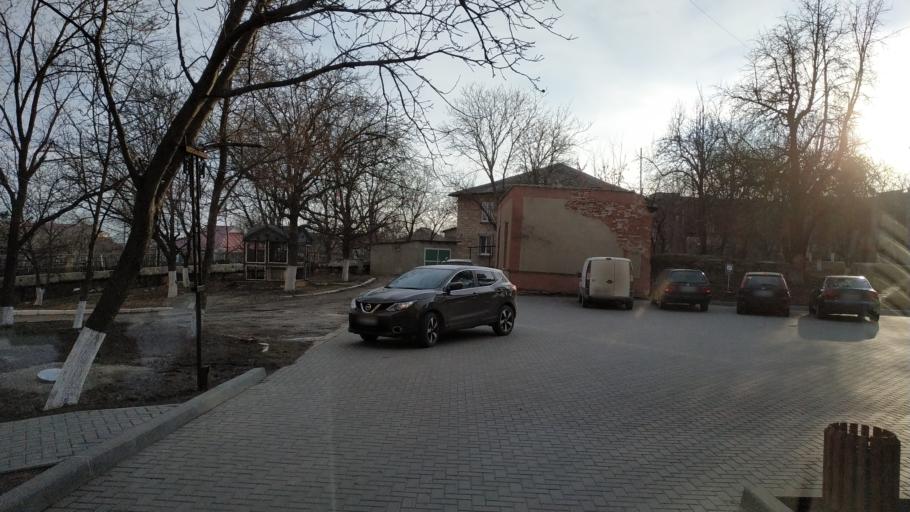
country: MD
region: Nisporeni
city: Nisporeni
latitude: 47.0871
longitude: 28.1766
